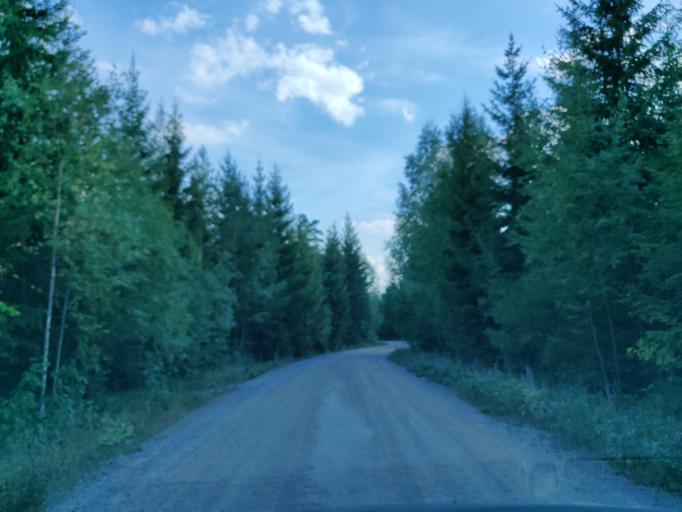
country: SE
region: Vaermland
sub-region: Hagfors Kommun
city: Hagfors
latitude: 60.0181
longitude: 13.6762
